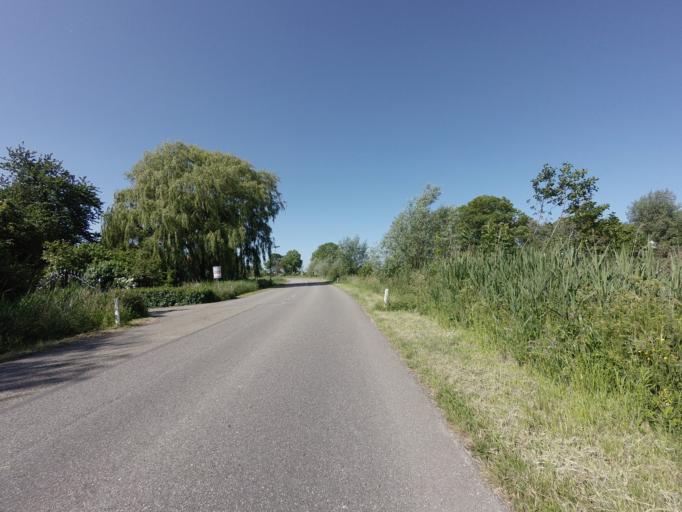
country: NL
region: Utrecht
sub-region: Stichtse Vecht
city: Vreeland
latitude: 52.2357
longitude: 4.9937
